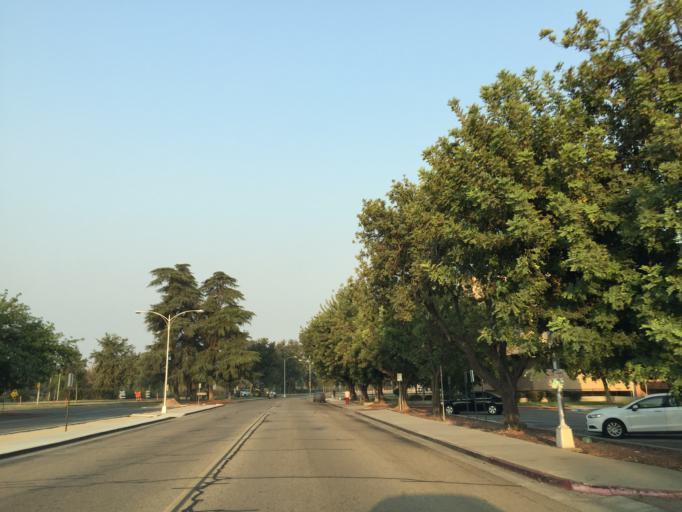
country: US
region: California
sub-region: Tulare County
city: Visalia
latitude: 36.3282
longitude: -119.3149
